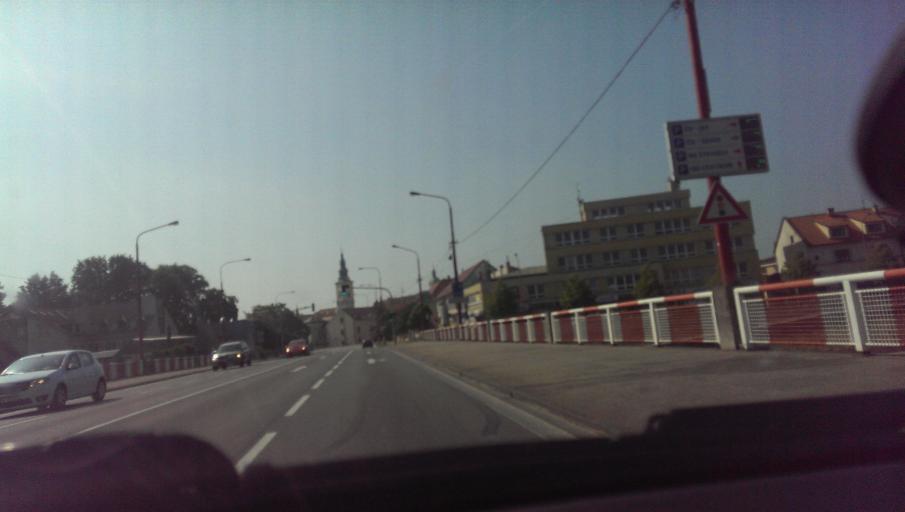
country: CZ
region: Zlin
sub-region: Okres Uherske Hradiste
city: Uherske Hradiste
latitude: 49.0734
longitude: 17.4586
